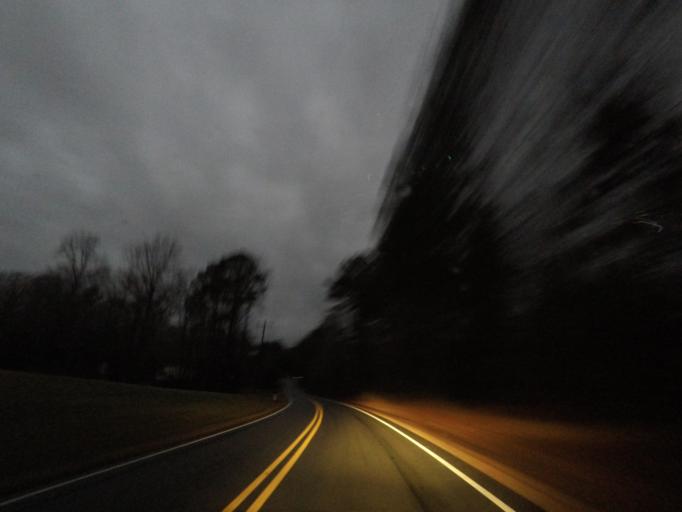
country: US
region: North Carolina
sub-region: Durham County
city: Durham
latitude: 36.0663
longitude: -78.9824
